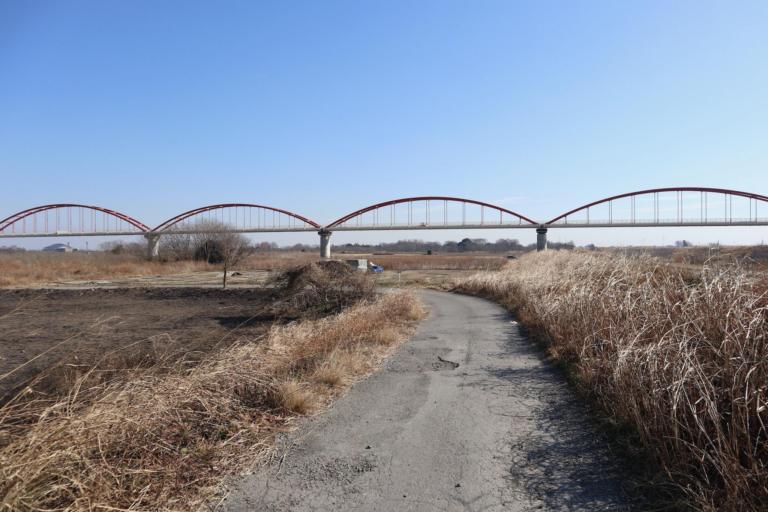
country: JP
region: Saitama
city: Fukiage-fujimi
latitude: 36.0821
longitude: 139.4375
